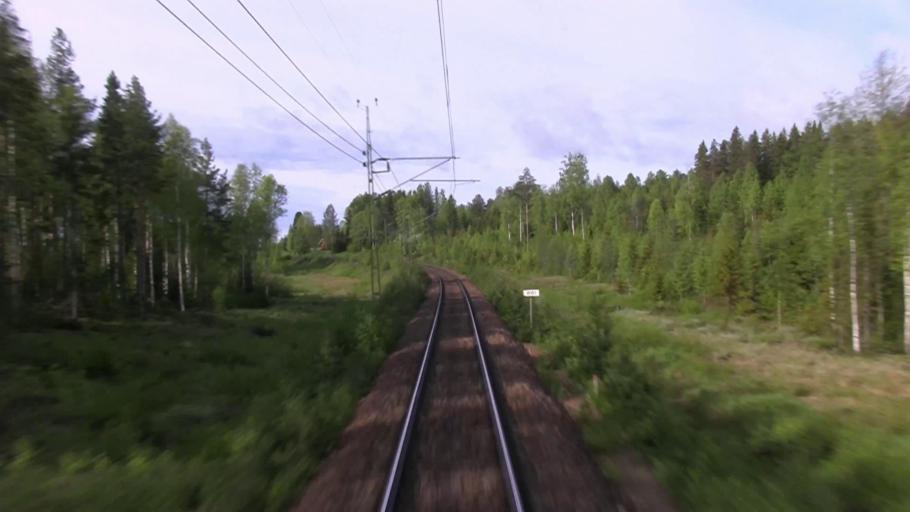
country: SE
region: Vaesterbotten
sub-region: Vindelns Kommun
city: Vindeln
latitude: 64.1093
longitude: 19.6874
